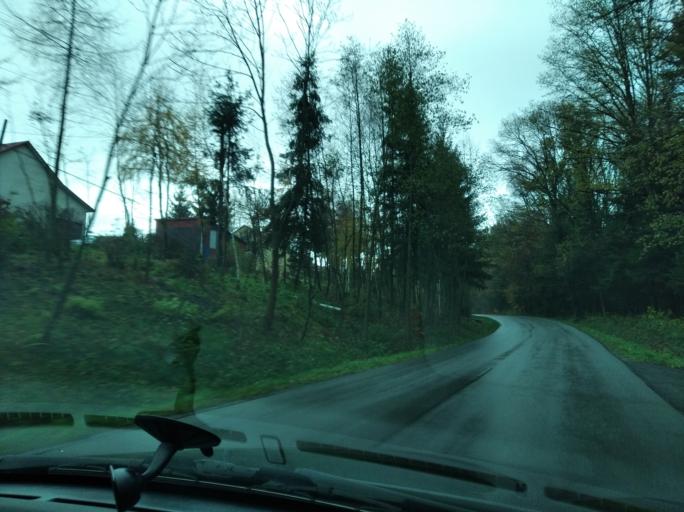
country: PL
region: Subcarpathian Voivodeship
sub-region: Powiat rzeszowski
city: Lecka
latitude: 49.9014
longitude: 22.0162
